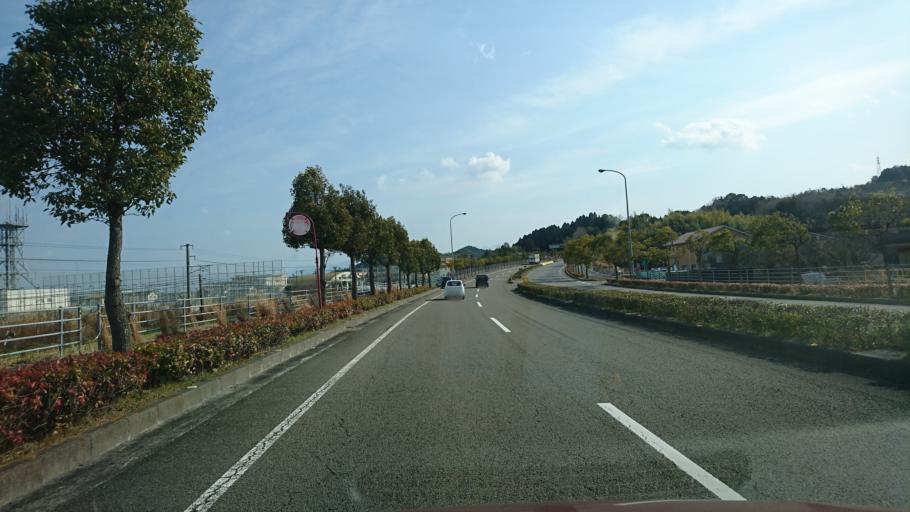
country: JP
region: Ehime
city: Saijo
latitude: 34.0183
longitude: 133.0300
